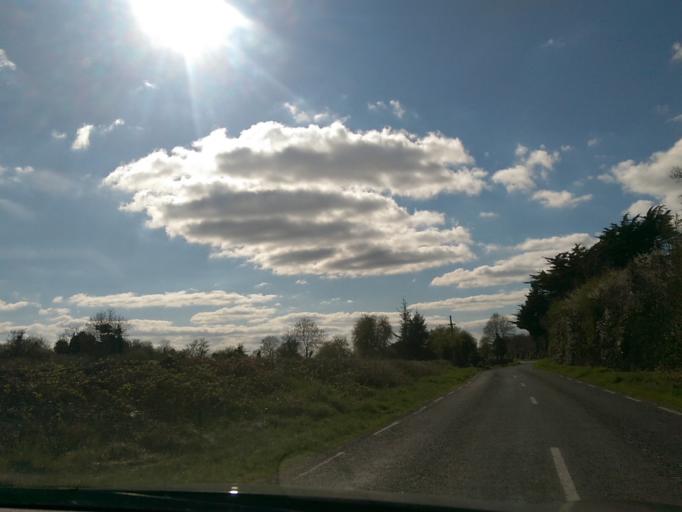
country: IE
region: Leinster
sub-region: Uibh Fhaili
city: Birr
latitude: 53.1030
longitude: -7.7639
